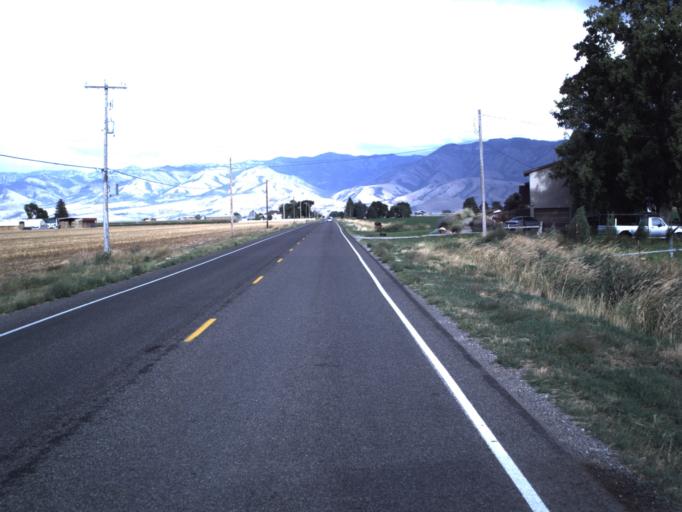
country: US
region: Utah
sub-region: Cache County
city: Lewiston
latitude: 41.9754
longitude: -111.9240
